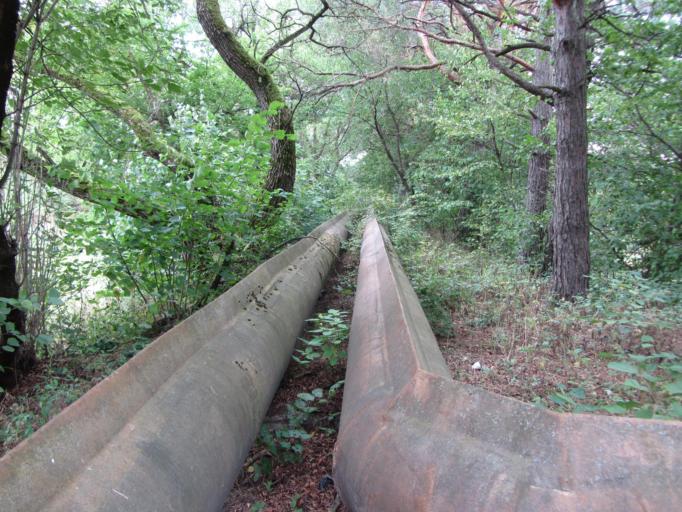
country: LT
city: Grigiskes
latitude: 54.6737
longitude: 25.0935
